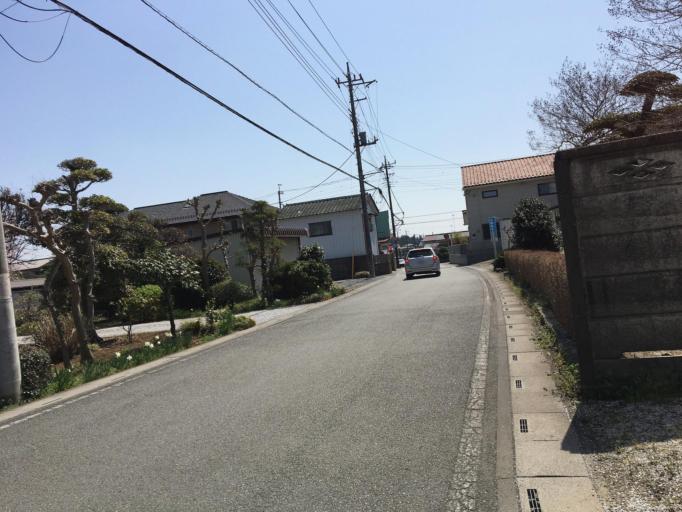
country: JP
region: Saitama
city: Sakado
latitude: 35.8997
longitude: 139.3623
